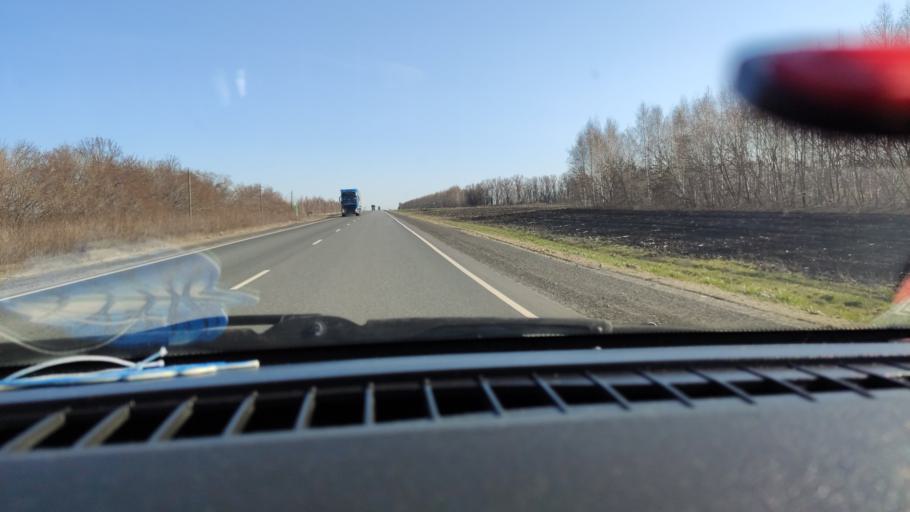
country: RU
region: Samara
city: Syzran'
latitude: 52.9847
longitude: 48.3160
